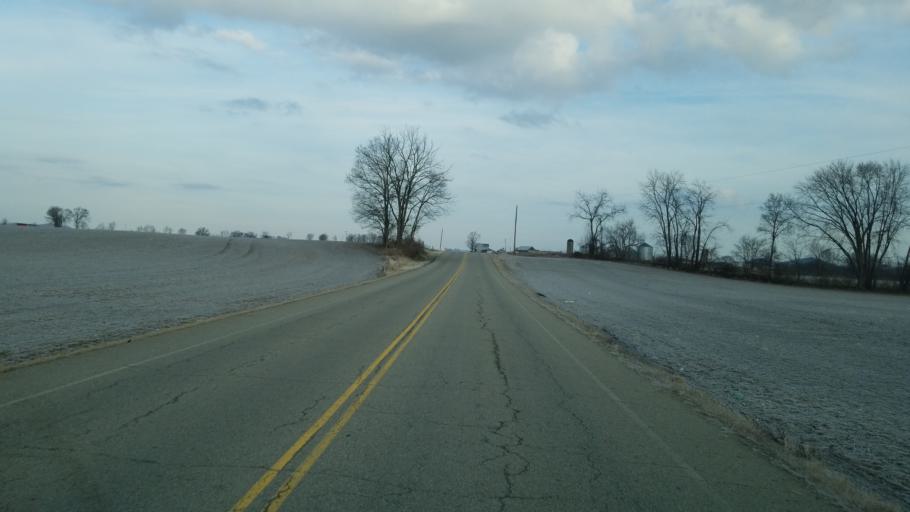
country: US
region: Ohio
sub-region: Ross County
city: Chillicothe
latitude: 39.2329
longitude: -82.8593
